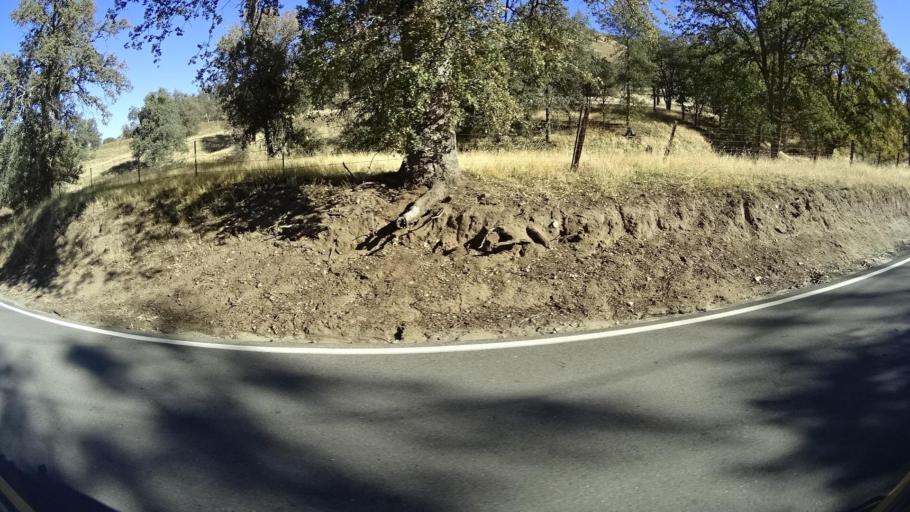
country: US
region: California
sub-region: Kern County
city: Alta Sierra
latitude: 35.7226
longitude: -118.6960
